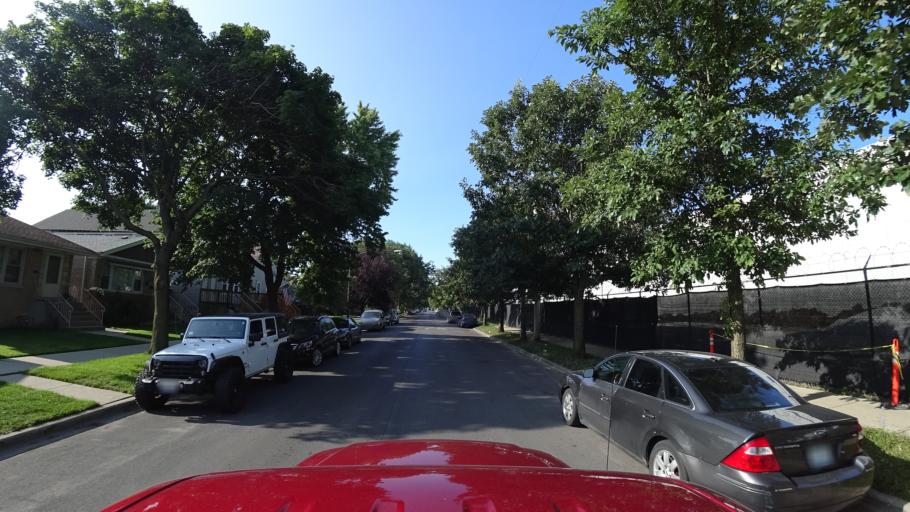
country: US
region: Illinois
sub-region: Cook County
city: Cicero
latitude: 41.7987
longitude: -87.7111
